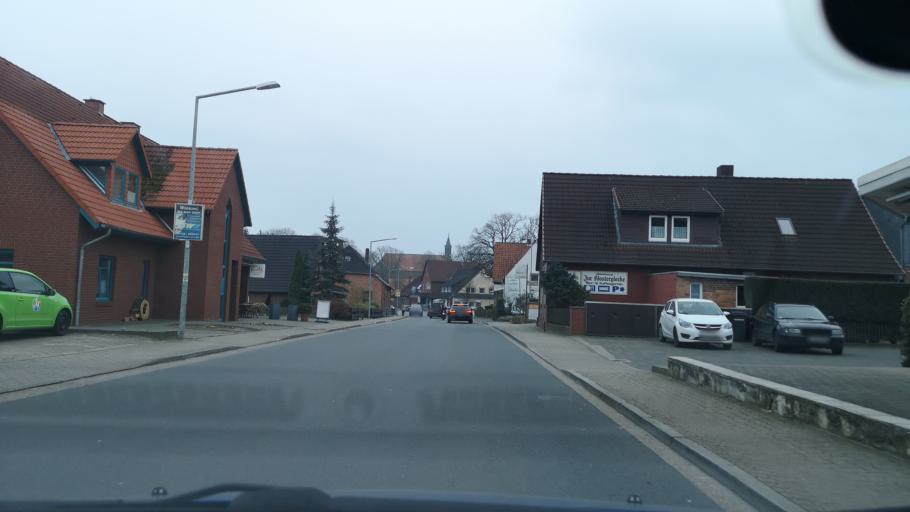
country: DE
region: Lower Saxony
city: Neustadt am Rubenberge
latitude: 52.5617
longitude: 9.4869
